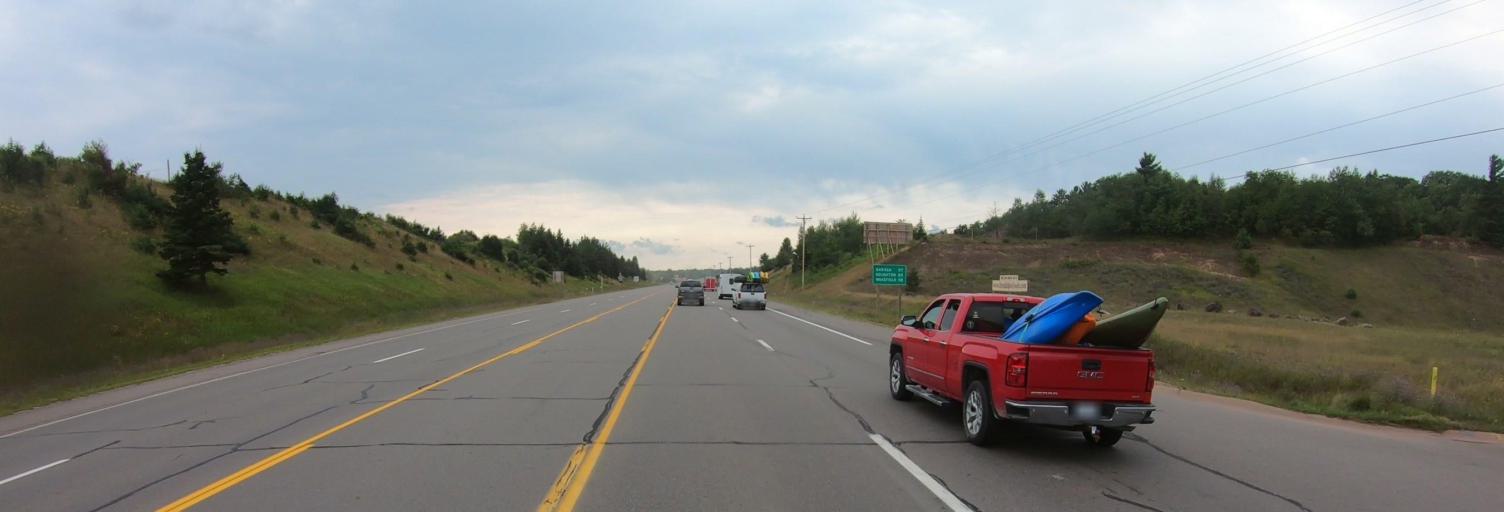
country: US
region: Michigan
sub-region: Marquette County
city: Ishpeming
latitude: 46.4979
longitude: -87.6854
